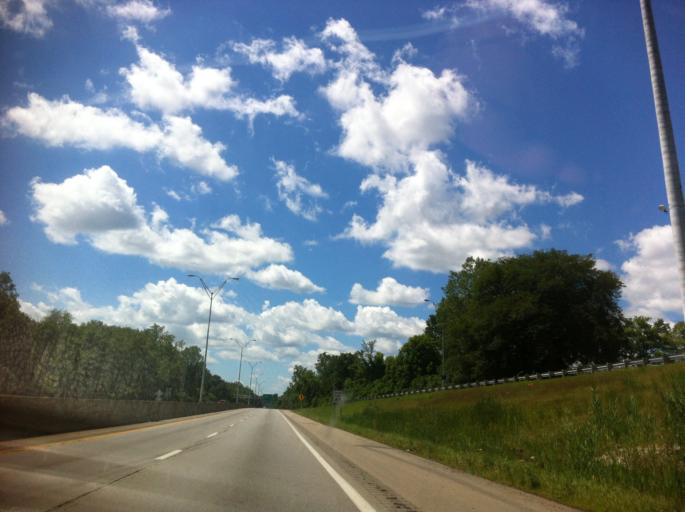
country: US
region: Ohio
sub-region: Lucas County
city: Ottawa Hills
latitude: 41.6901
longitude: -83.6639
